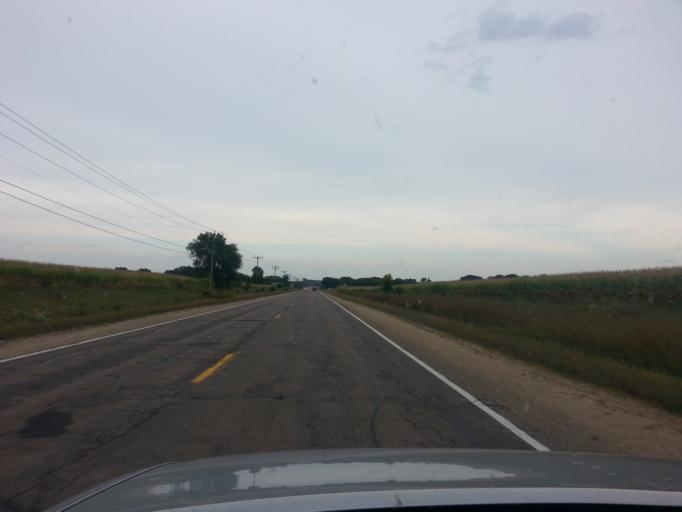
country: US
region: Minnesota
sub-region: Washington County
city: Lake Elmo
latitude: 44.9452
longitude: -92.8766
